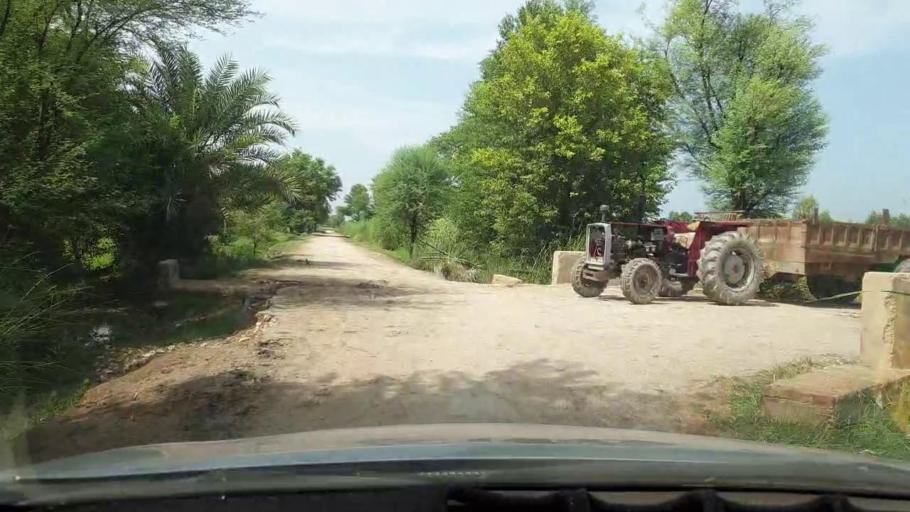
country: PK
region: Sindh
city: Khairpur
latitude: 27.4859
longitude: 68.7506
